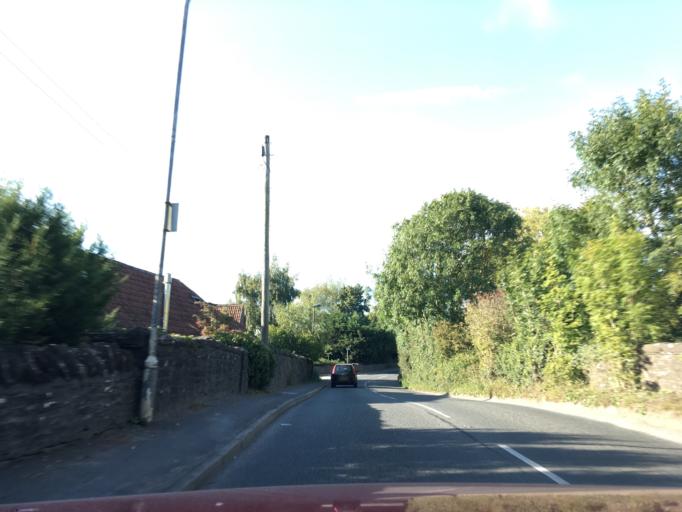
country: GB
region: England
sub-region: South Gloucestershire
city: Yate
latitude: 51.5184
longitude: -2.4345
